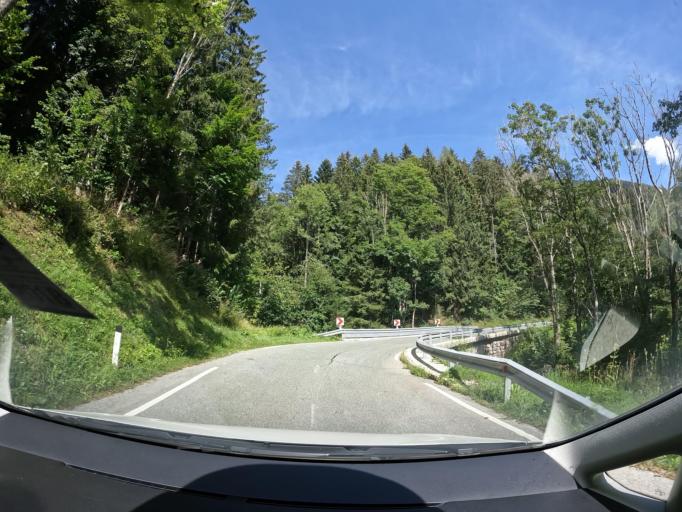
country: AT
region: Carinthia
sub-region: Politischer Bezirk Feldkirchen
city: Glanegg
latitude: 46.7379
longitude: 14.1968
